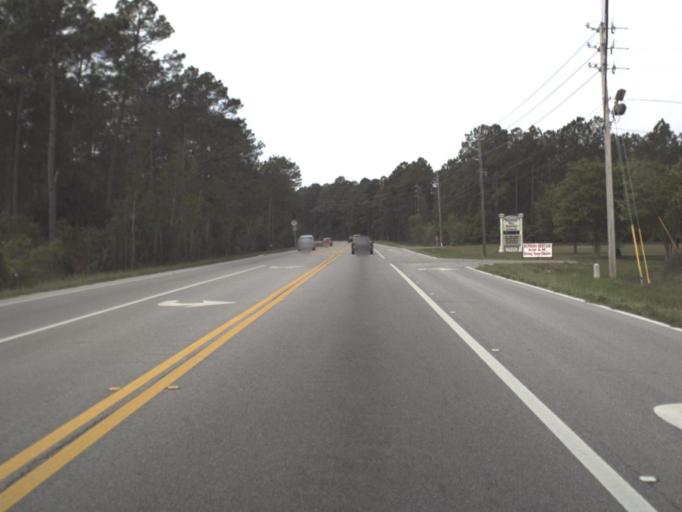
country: US
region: Florida
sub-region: Escambia County
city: Myrtle Grove
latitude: 30.3389
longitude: -87.4071
